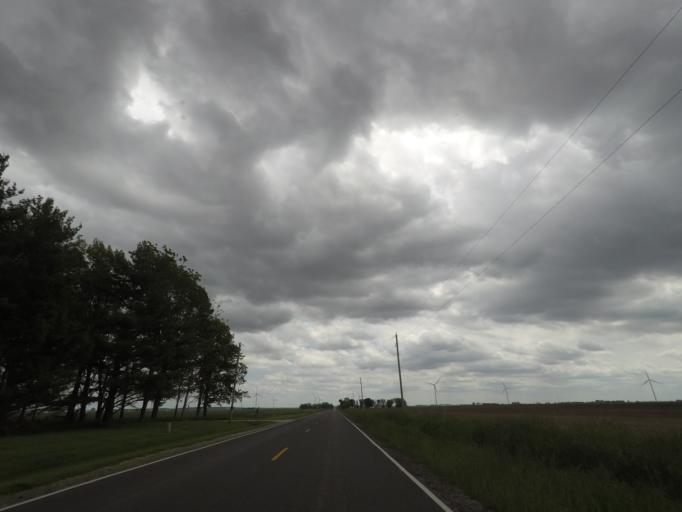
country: US
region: Illinois
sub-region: Macon County
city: Warrensburg
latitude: 39.9865
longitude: -89.0857
